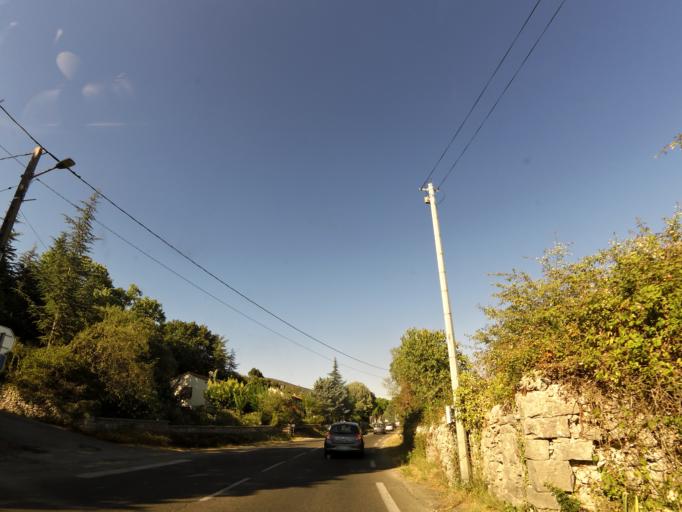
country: FR
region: Languedoc-Roussillon
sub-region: Departement du Gard
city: Saint-Hippolyte-du-Fort
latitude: 43.9617
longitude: 3.8485
